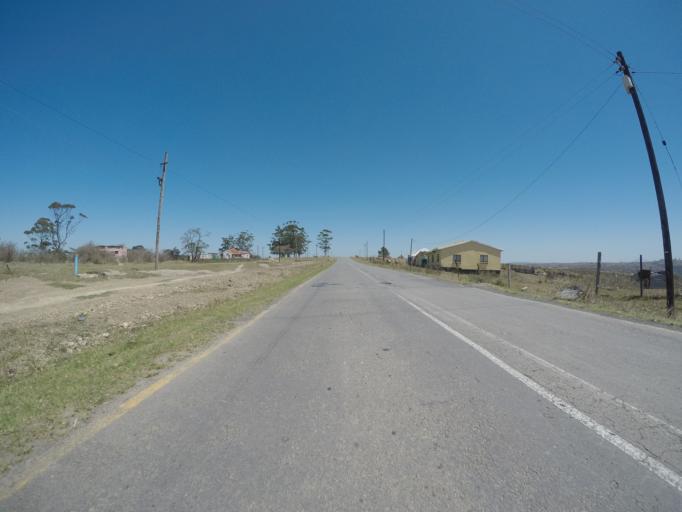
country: ZA
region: Eastern Cape
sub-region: OR Tambo District Municipality
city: Libode
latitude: -31.9167
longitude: 28.9807
